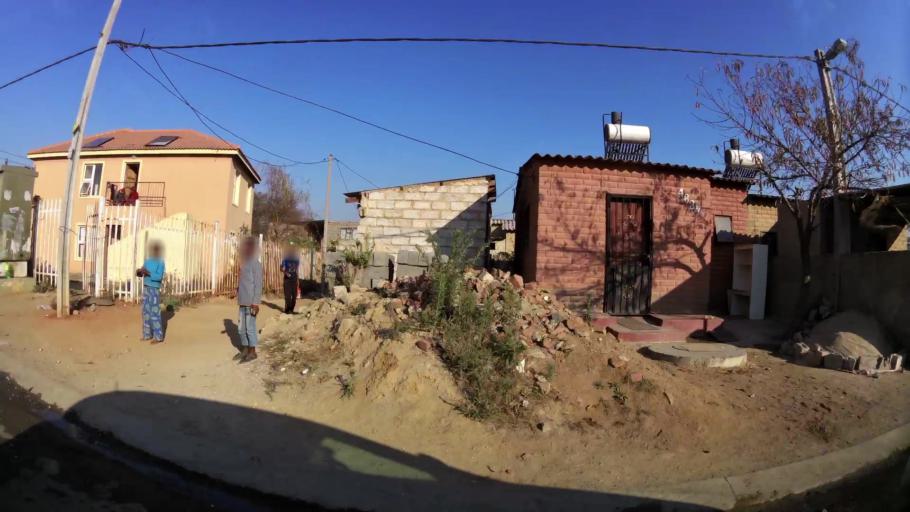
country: ZA
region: Gauteng
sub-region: City of Johannesburg Metropolitan Municipality
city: Modderfontein
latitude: -26.0879
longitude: 28.1096
